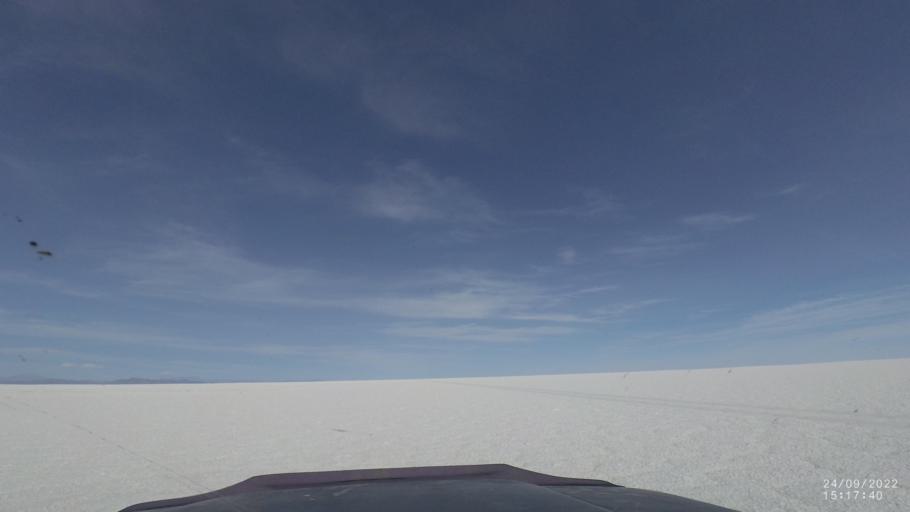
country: BO
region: Potosi
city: Colchani
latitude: -19.9910
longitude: -67.4253
